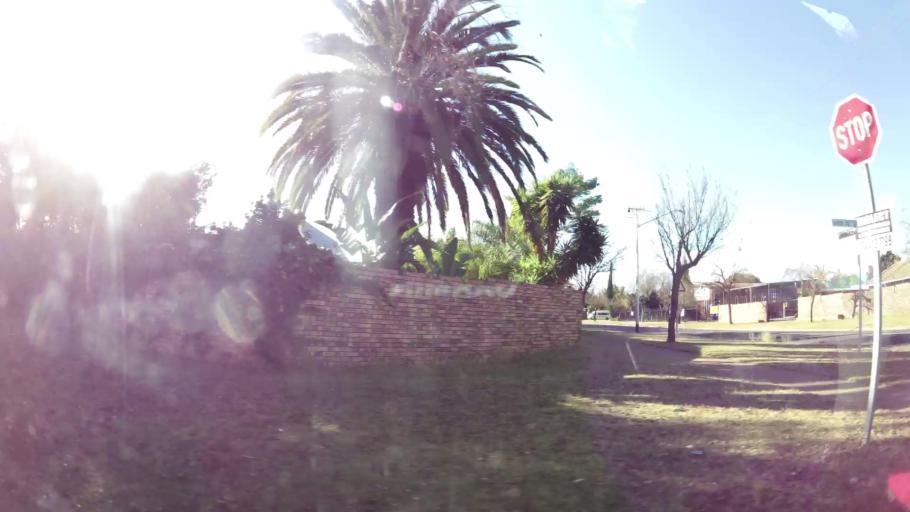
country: ZA
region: Gauteng
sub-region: City of Tshwane Metropolitan Municipality
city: Pretoria
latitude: -25.7087
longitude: 28.2508
